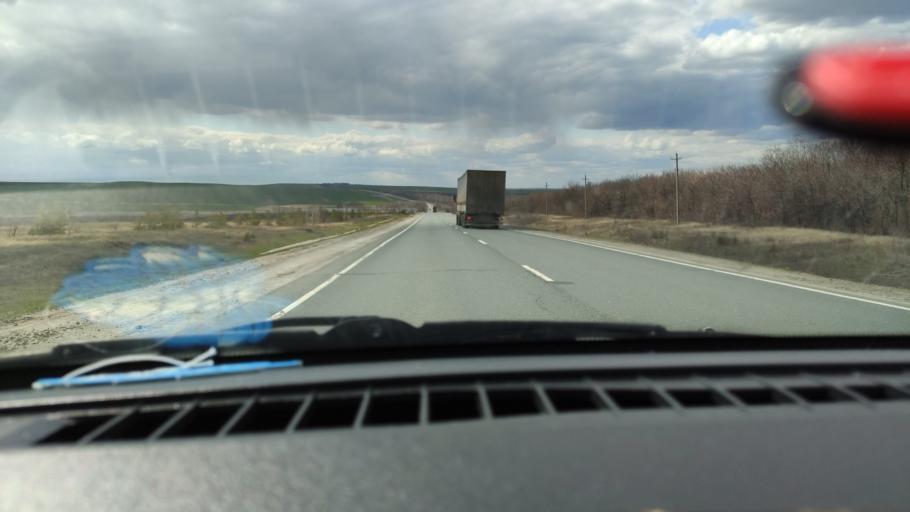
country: RU
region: Saratov
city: Alekseyevka
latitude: 52.2527
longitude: 47.9139
